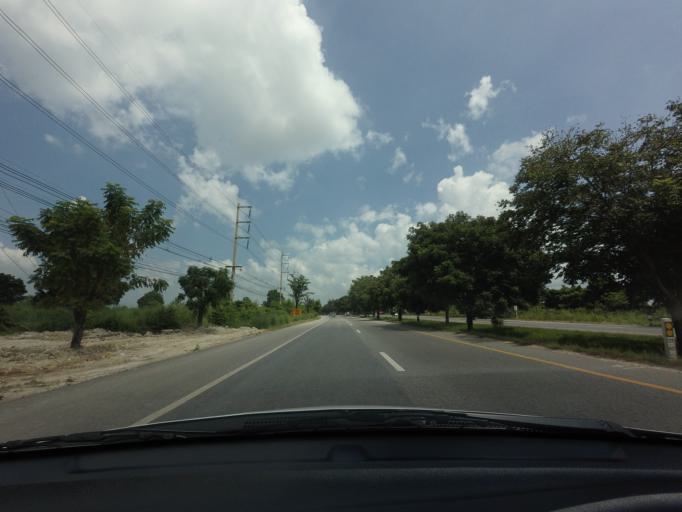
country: TH
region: Chachoengsao
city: Sanam Chai Khet
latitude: 13.7895
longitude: 101.5376
